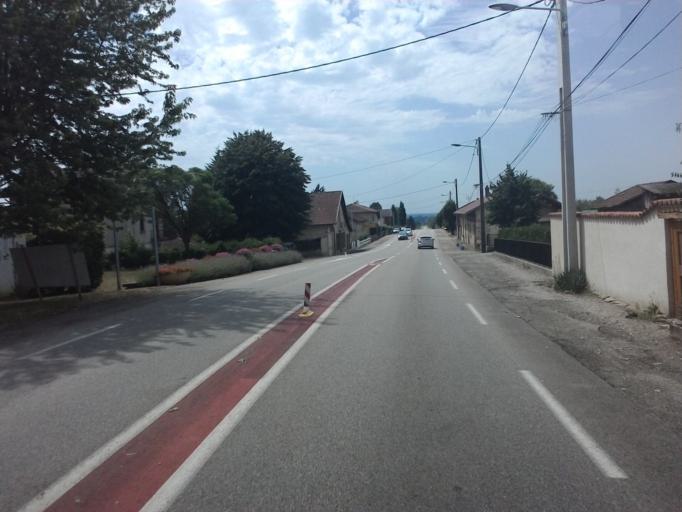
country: FR
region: Rhone-Alpes
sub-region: Departement de l'Ain
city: Coligny
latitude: 46.3789
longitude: 5.3442
